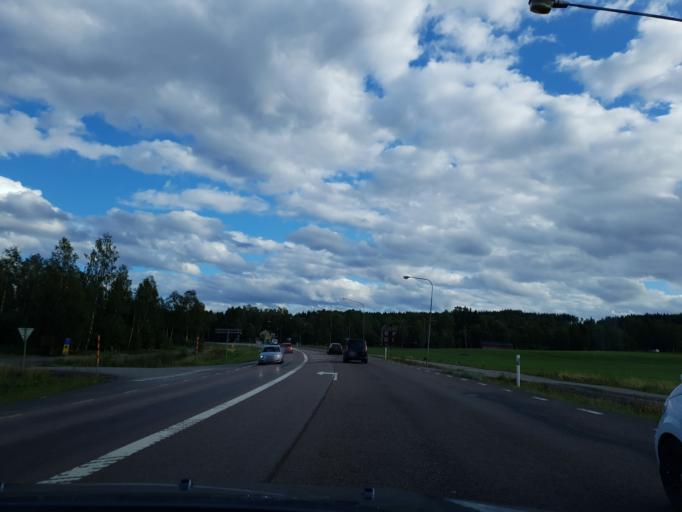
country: SE
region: Vaesternorrland
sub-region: Haernoesands Kommun
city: Haernoesand
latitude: 62.6686
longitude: 17.8412
